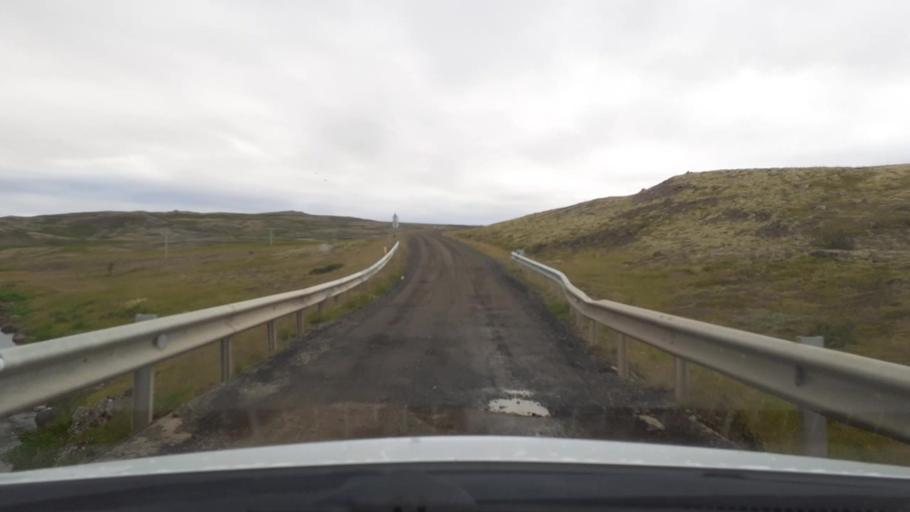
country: IS
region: Capital Region
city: Mosfellsbaer
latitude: 64.2069
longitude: -21.5659
